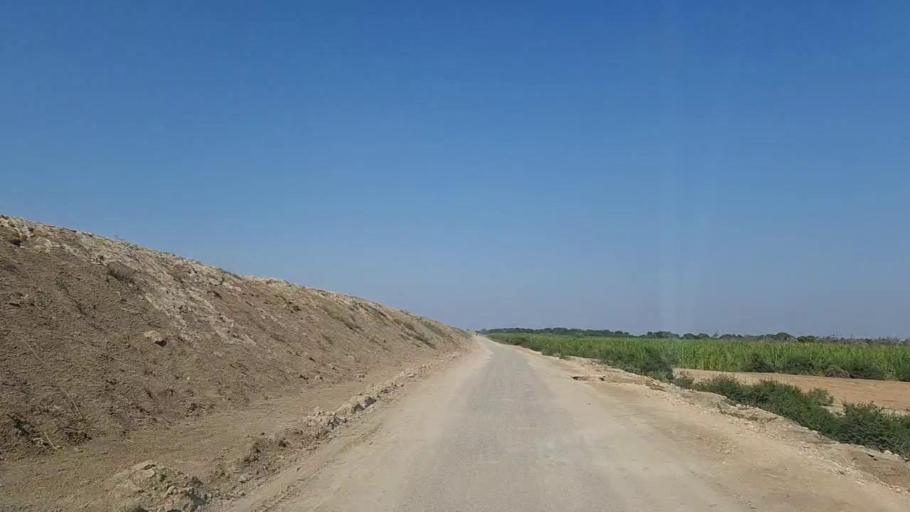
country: PK
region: Sindh
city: Chuhar Jamali
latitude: 24.5630
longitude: 68.0286
